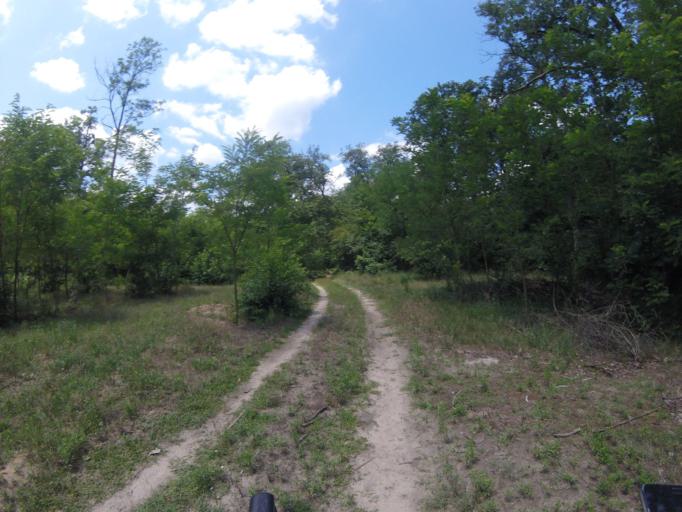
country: HU
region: Pest
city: Csemo
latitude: 47.0710
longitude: 19.7289
